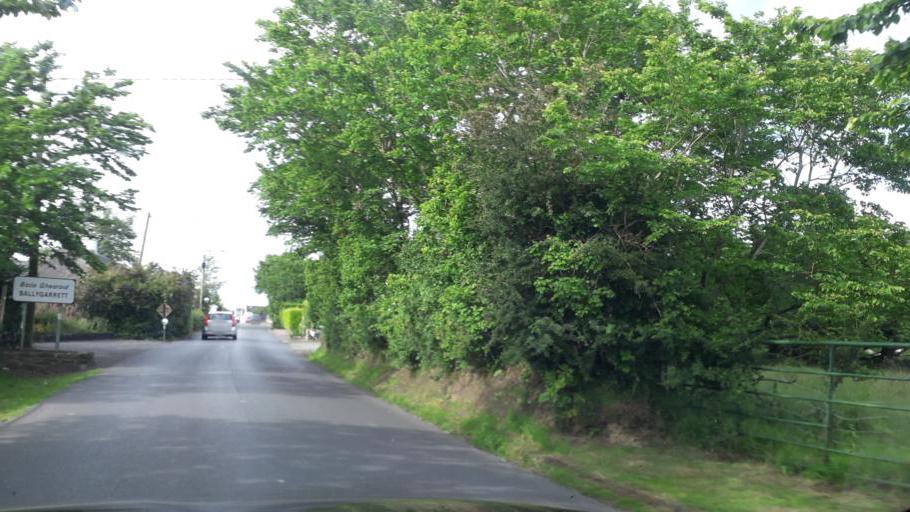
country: IE
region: Leinster
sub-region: Loch Garman
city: Courtown
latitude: 52.5716
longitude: -6.2305
